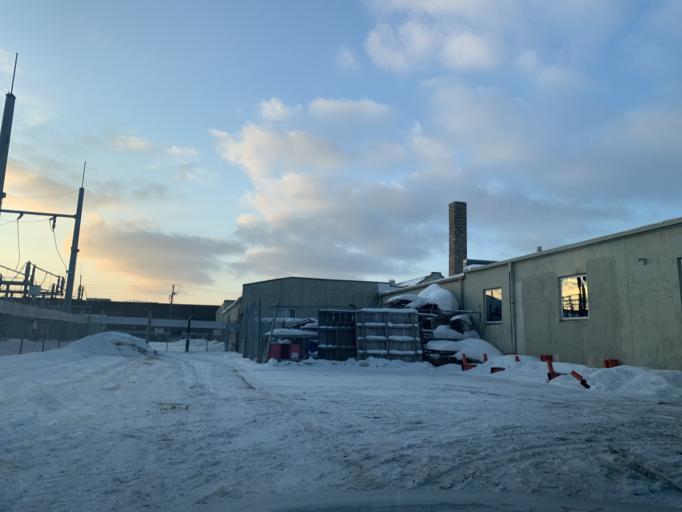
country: US
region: Minnesota
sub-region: Hennepin County
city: Minneapolis
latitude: 44.9779
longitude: -93.2903
